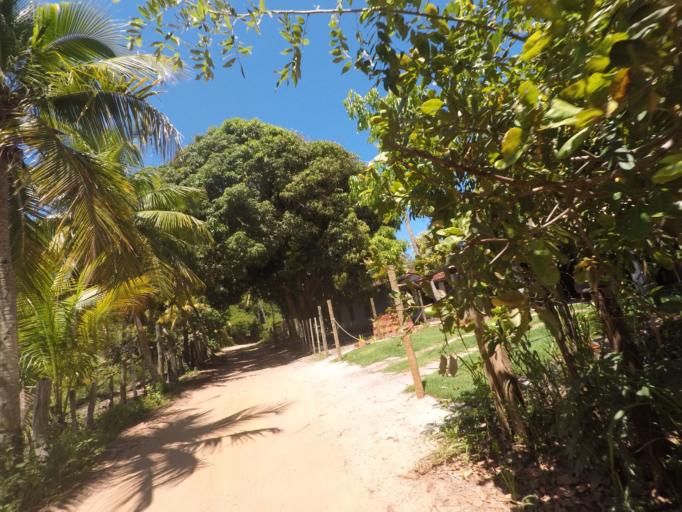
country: BR
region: Bahia
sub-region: Marau
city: Marau
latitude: -14.0236
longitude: -38.9496
